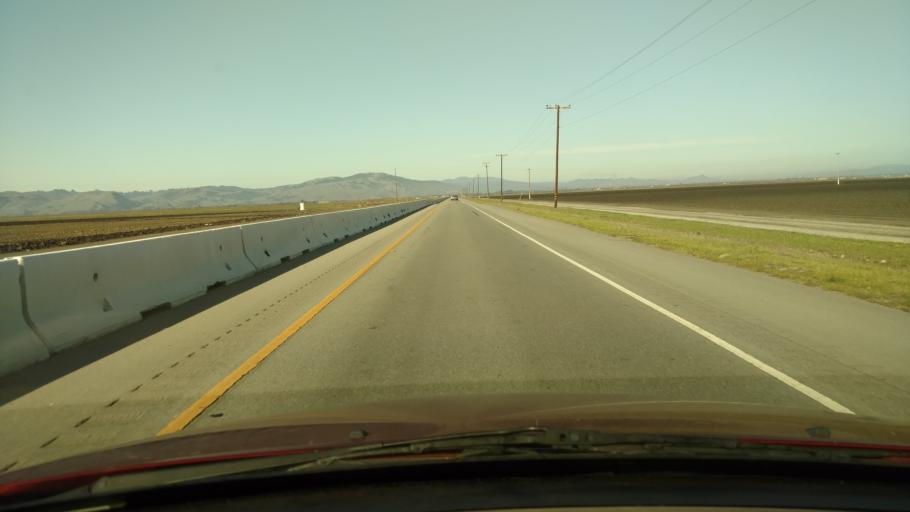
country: US
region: California
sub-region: San Benito County
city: Hollister
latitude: 36.9262
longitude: -121.4651
